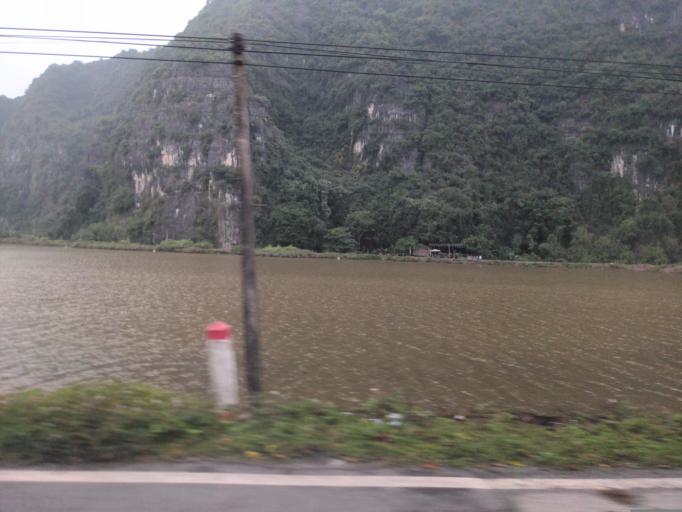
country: VN
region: Ninh Binh
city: Thi Tran Tam Diep
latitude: 20.2209
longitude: 105.9257
